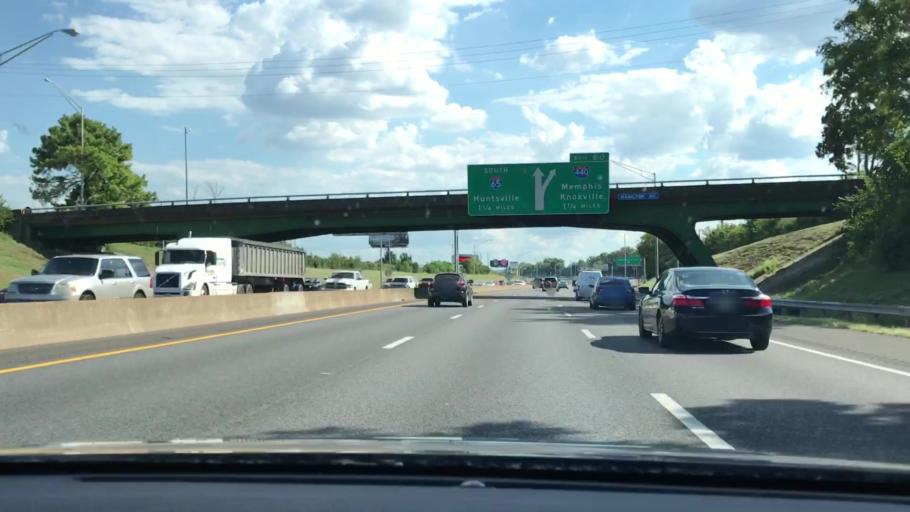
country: US
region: Tennessee
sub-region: Davidson County
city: Nashville
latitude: 36.1385
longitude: -86.7764
